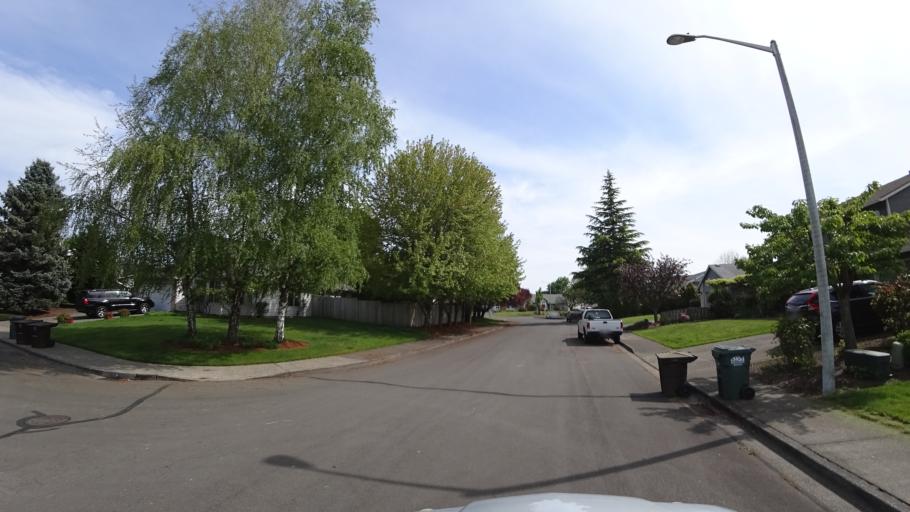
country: US
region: Oregon
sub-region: Washington County
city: Rockcreek
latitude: 45.5371
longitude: -122.9287
